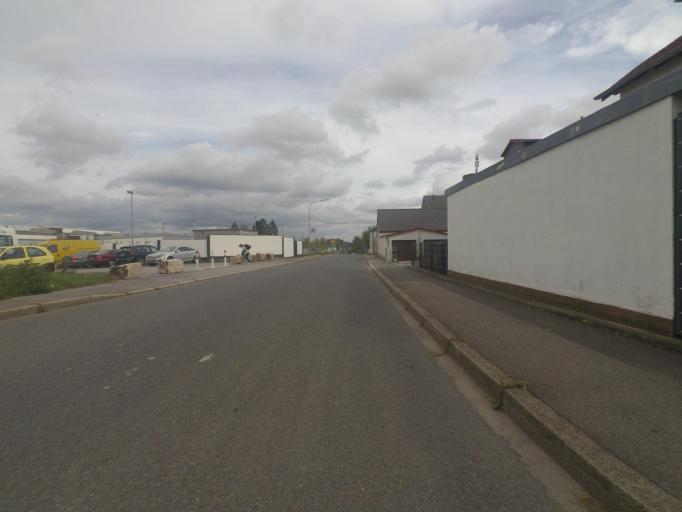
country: DE
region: North Rhine-Westphalia
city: Iserlohn
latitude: 51.4232
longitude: 7.6695
